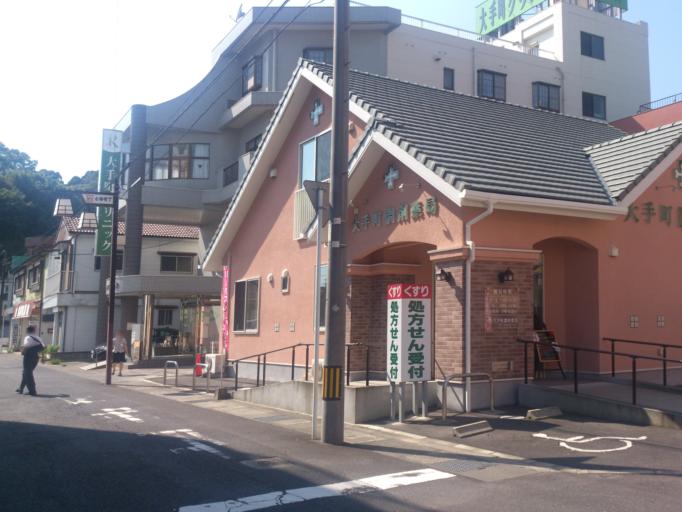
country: JP
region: Kagoshima
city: Kanoya
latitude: 31.3891
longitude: 130.8496
